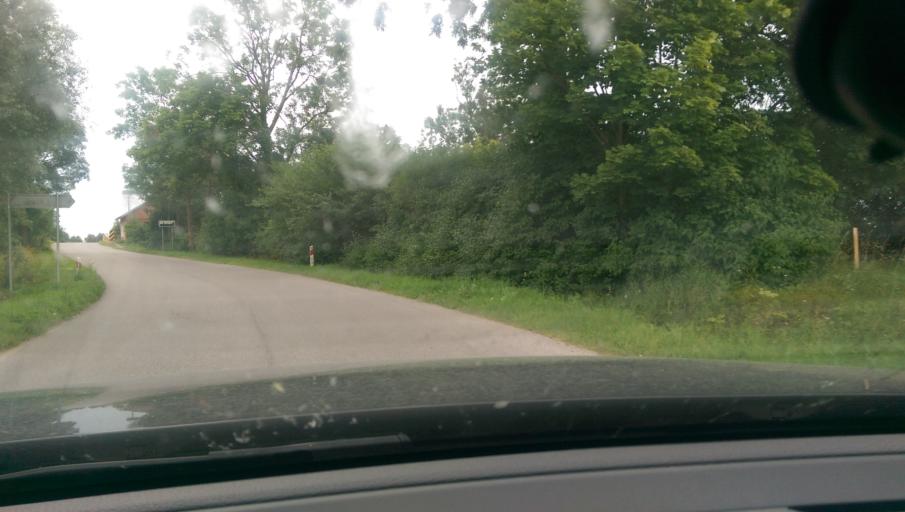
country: PL
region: Podlasie
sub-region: Powiat suwalski
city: Raczki
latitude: 53.9095
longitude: 22.7160
